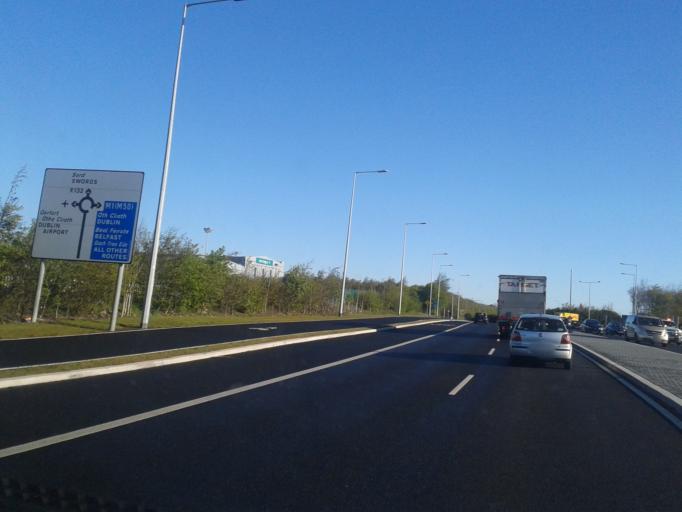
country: IE
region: Leinster
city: Kinsealy-Drinan
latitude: 53.4259
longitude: -6.2295
